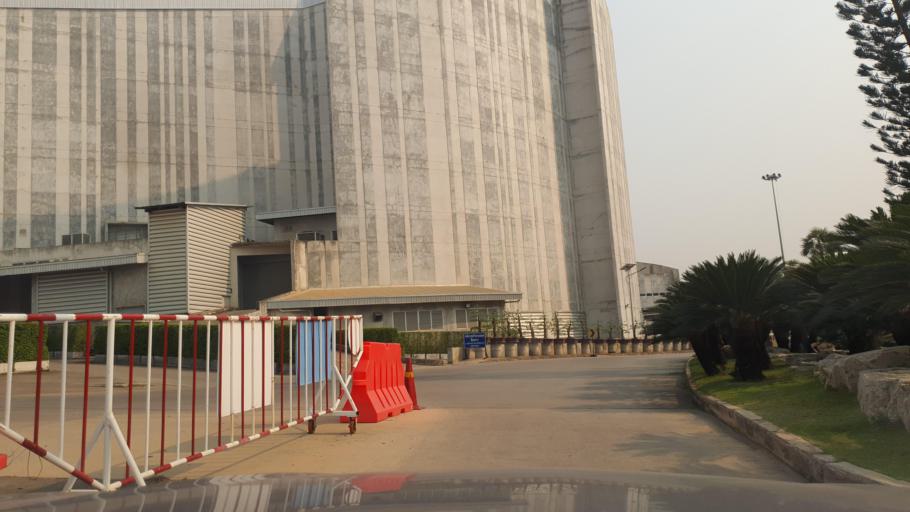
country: TH
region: Chon Buri
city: Sattahip
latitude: 12.7693
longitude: 100.9324
